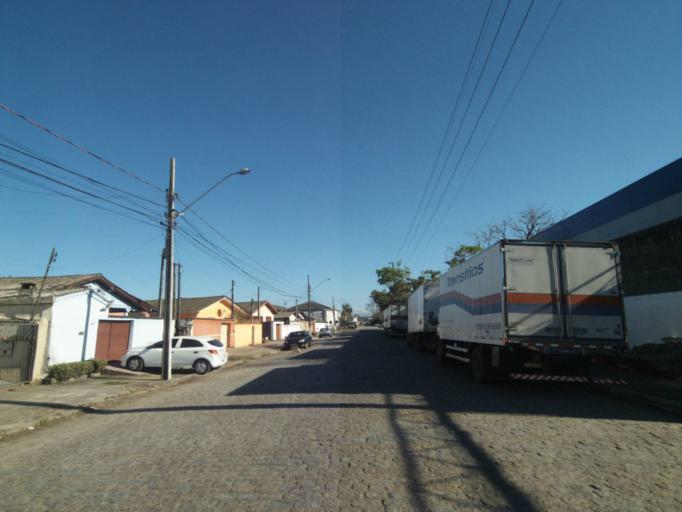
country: BR
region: Parana
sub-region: Paranagua
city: Paranagua
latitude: -25.5127
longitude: -48.5088
